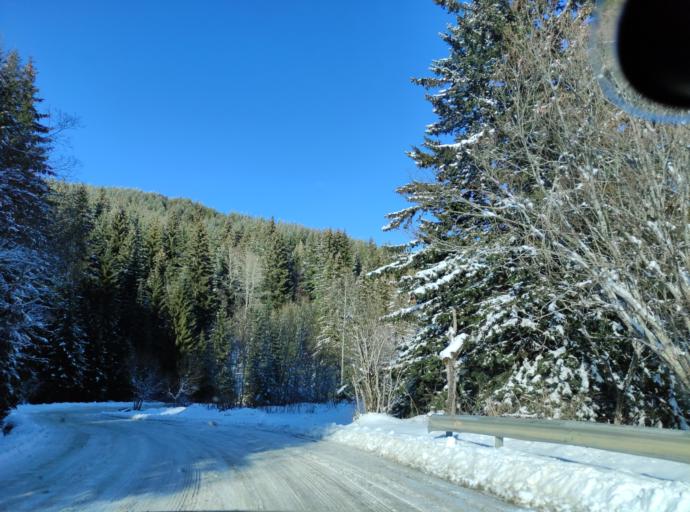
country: BG
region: Sofia-Capital
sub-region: Stolichna Obshtina
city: Sofia
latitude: 42.5873
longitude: 23.2977
